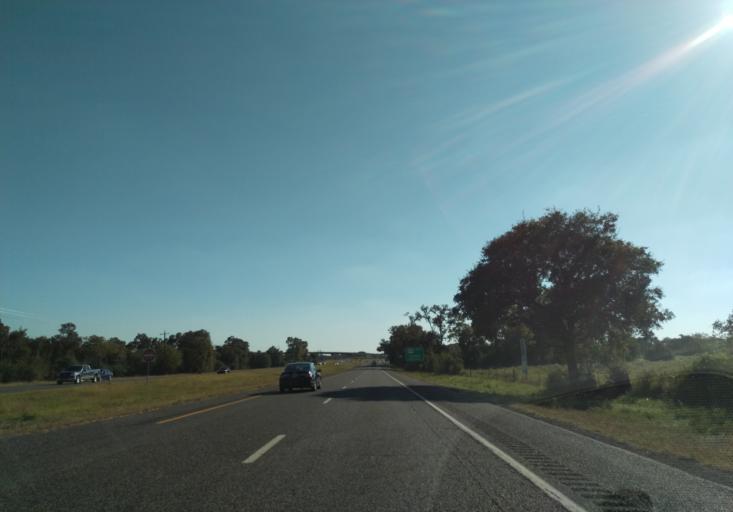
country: US
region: Texas
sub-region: Waller County
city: Hempstead
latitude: 30.1235
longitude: -96.0747
